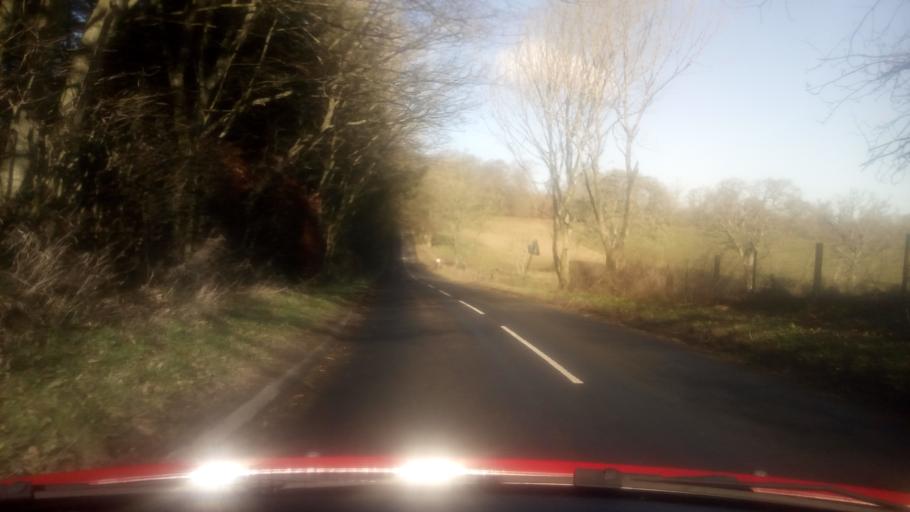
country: GB
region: Scotland
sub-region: The Scottish Borders
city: Newtown St Boswells
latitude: 55.5224
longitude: -2.7242
